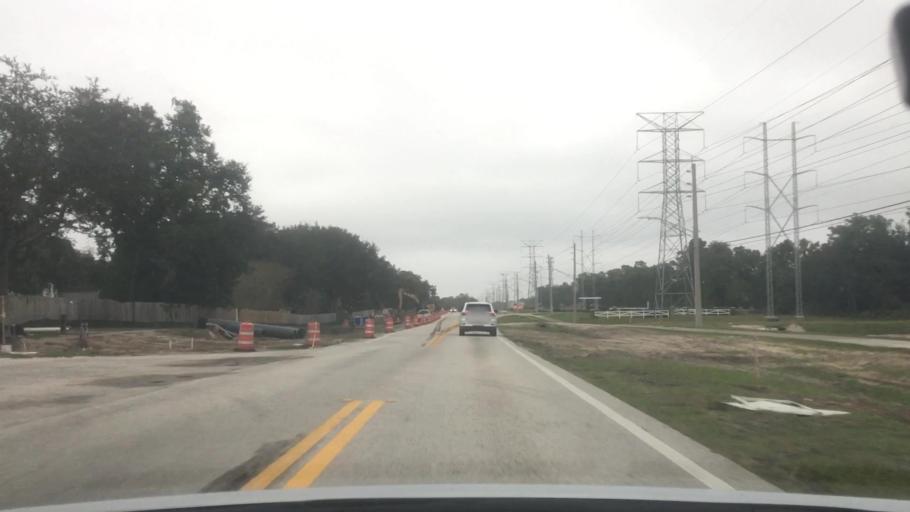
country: US
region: Florida
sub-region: Duval County
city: Atlantic Beach
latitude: 30.3524
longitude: -81.4900
